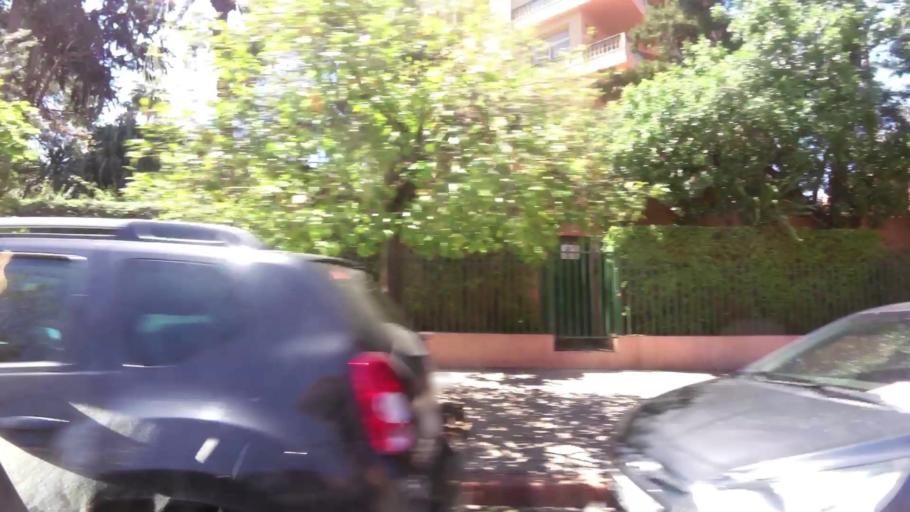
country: MA
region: Marrakech-Tensift-Al Haouz
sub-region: Marrakech
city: Marrakesh
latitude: 31.6224
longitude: -8.0039
